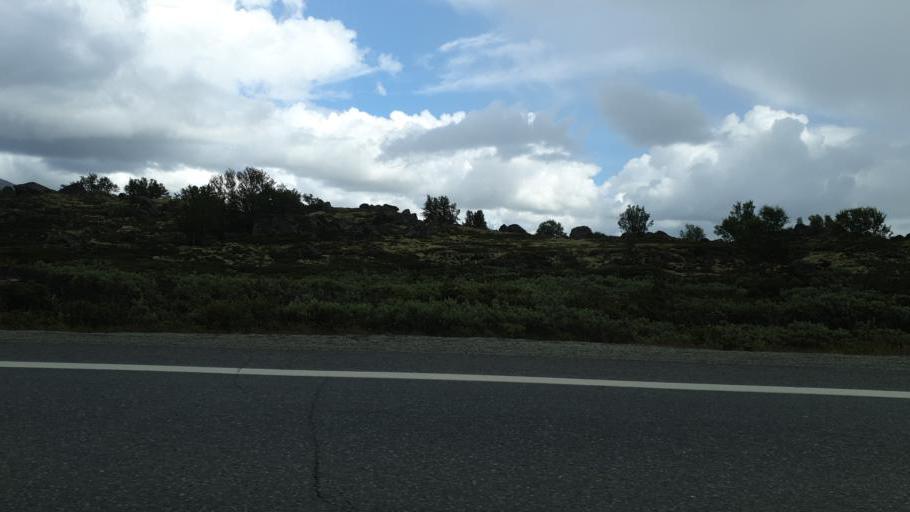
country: NO
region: Sor-Trondelag
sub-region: Oppdal
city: Oppdal
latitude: 62.2686
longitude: 9.5837
